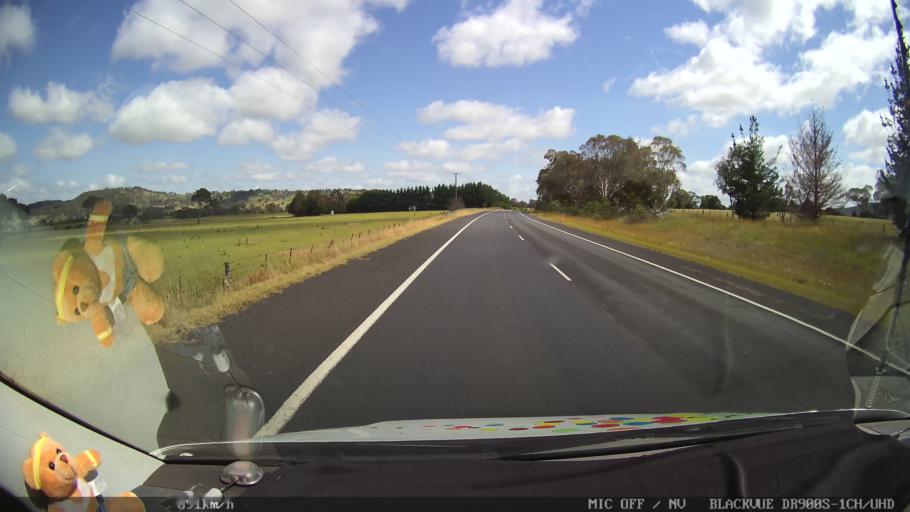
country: AU
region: New South Wales
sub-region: Glen Innes Severn
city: Glen Innes
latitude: -29.8790
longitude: 151.7340
